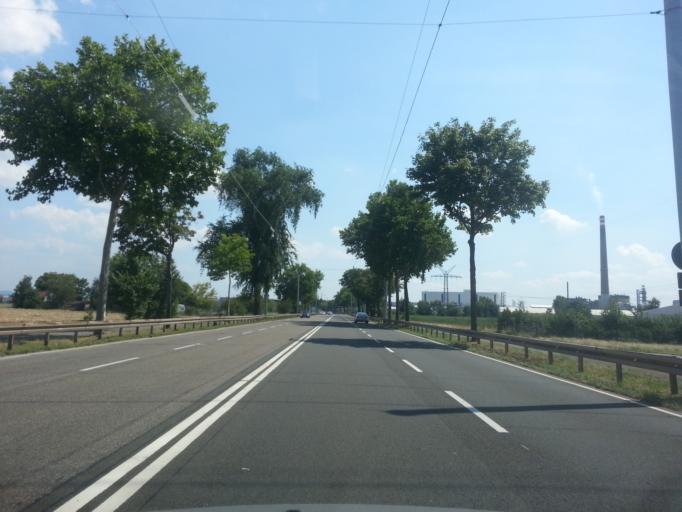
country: DE
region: Baden-Wuerttemberg
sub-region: Karlsruhe Region
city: Mannheim
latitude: 49.5430
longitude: 8.4605
